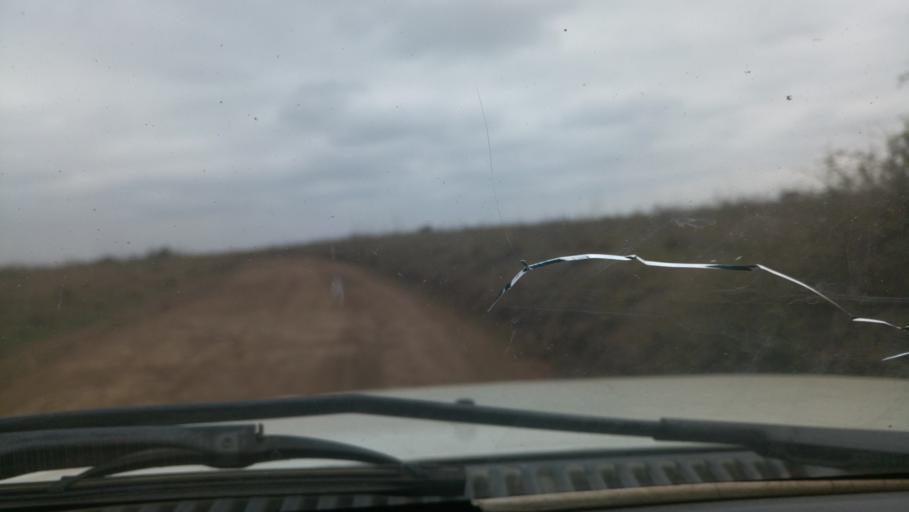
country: KE
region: Nairobi Area
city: Pumwani
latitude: -1.3830
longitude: 36.8694
